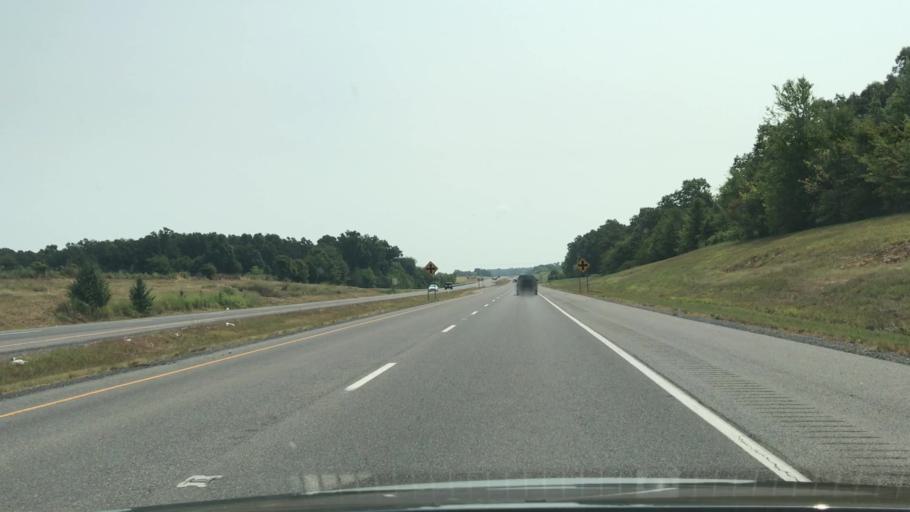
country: US
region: Kentucky
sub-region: Calloway County
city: Murray
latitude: 36.6505
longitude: -88.2661
